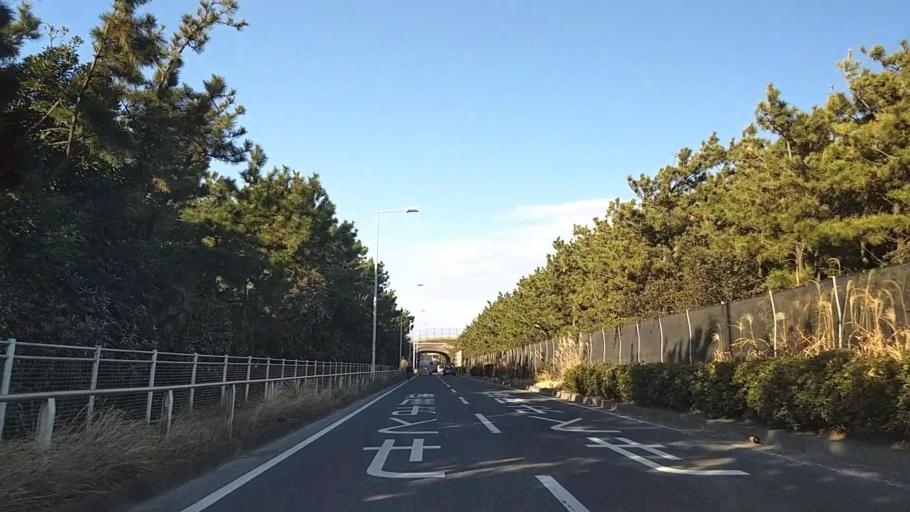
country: JP
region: Kanagawa
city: Fujisawa
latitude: 35.3196
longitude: 139.4491
